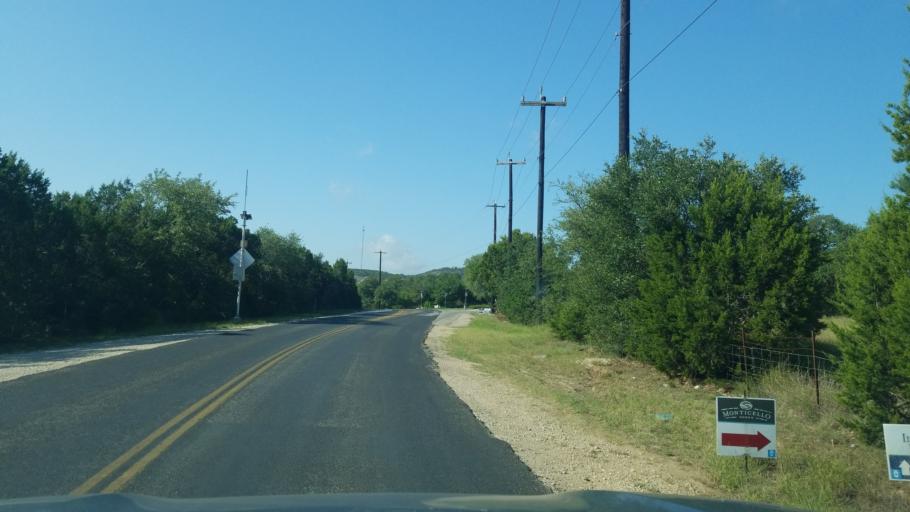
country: US
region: Texas
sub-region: Comal County
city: Bulverde
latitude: 29.7249
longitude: -98.4535
